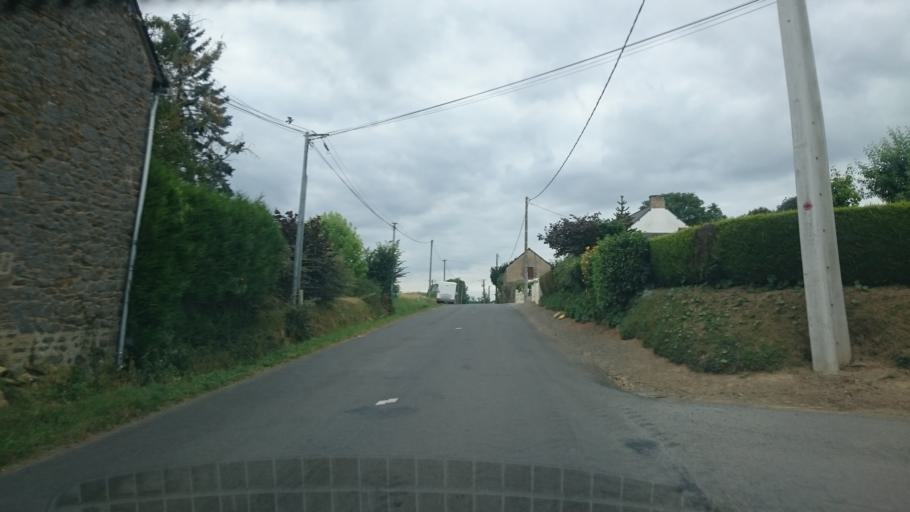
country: FR
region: Brittany
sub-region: Departement d'Ille-et-Vilaine
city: Saint-Domineuc
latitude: 48.4050
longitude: -1.8647
